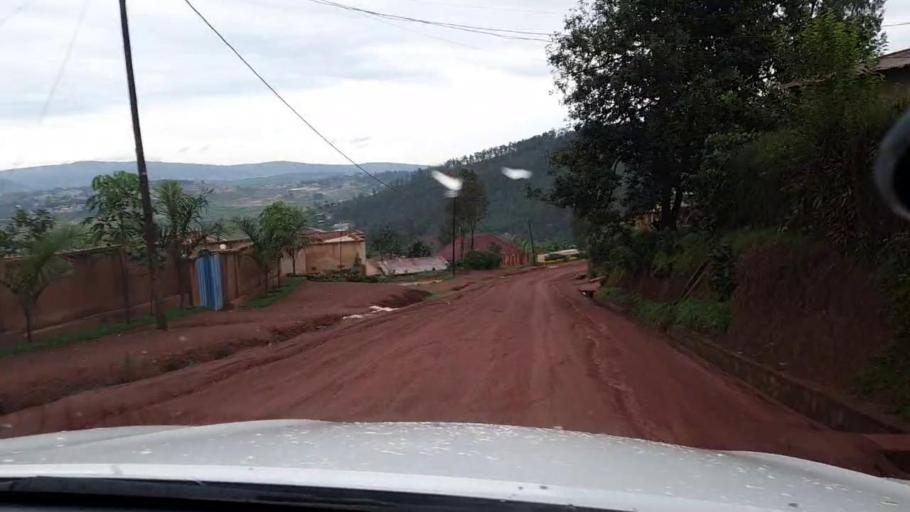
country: RW
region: Kigali
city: Kigali
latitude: -1.9044
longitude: 30.0447
